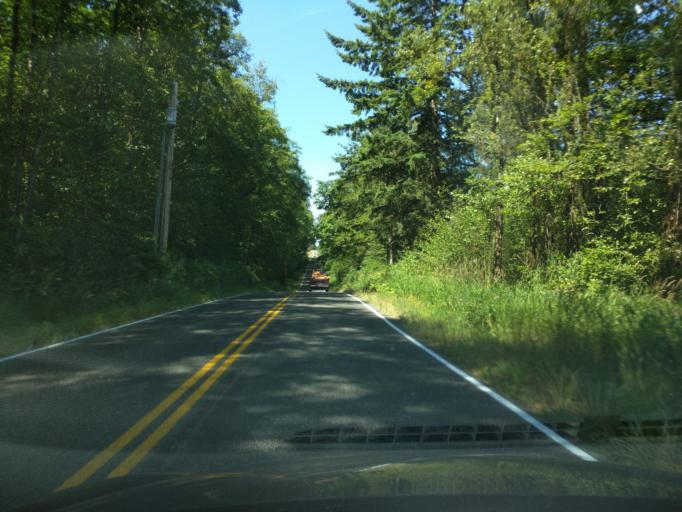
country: CA
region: British Columbia
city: Langley
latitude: 48.9934
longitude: -122.6265
